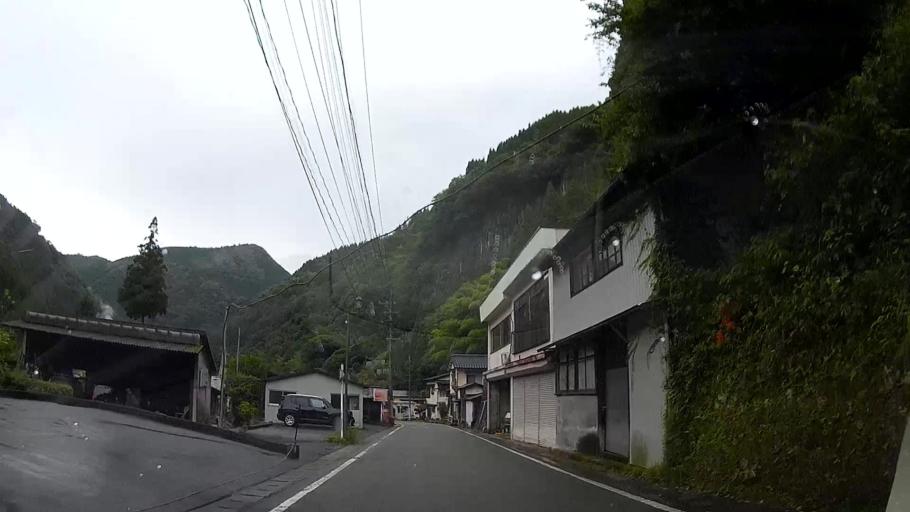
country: JP
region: Oita
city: Tsukawaki
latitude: 33.1803
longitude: 131.0372
